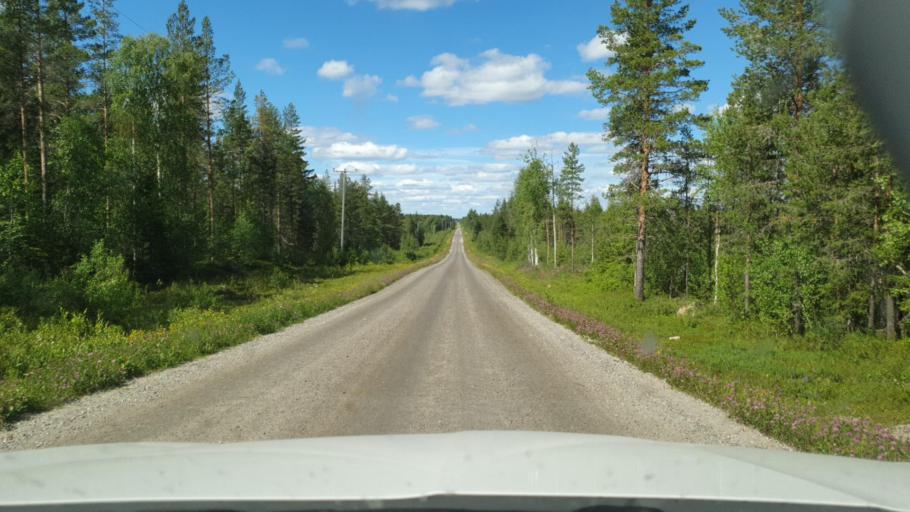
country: SE
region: Vaesterbotten
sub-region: Skelleftea Kommun
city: Backa
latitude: 65.1627
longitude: 21.1434
